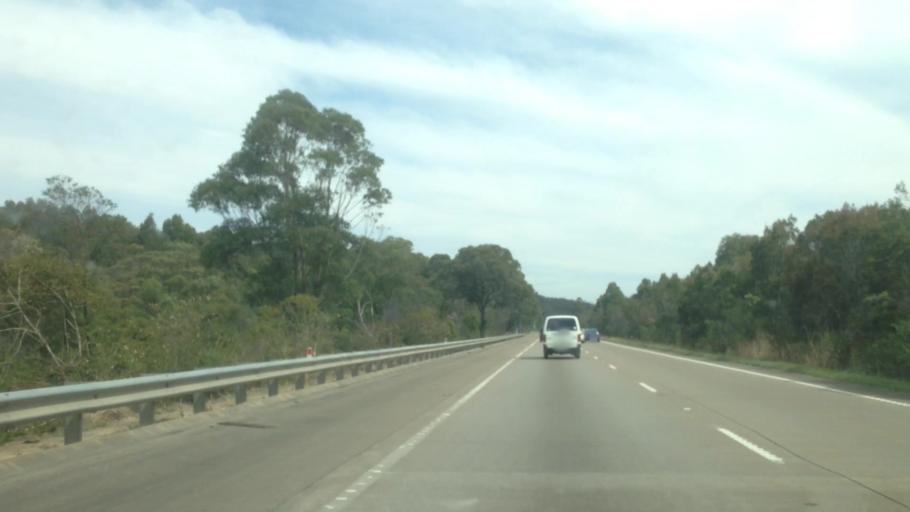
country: AU
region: New South Wales
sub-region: Lake Macquarie Shire
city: Fennell Bay
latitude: -32.9646
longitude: 151.5380
